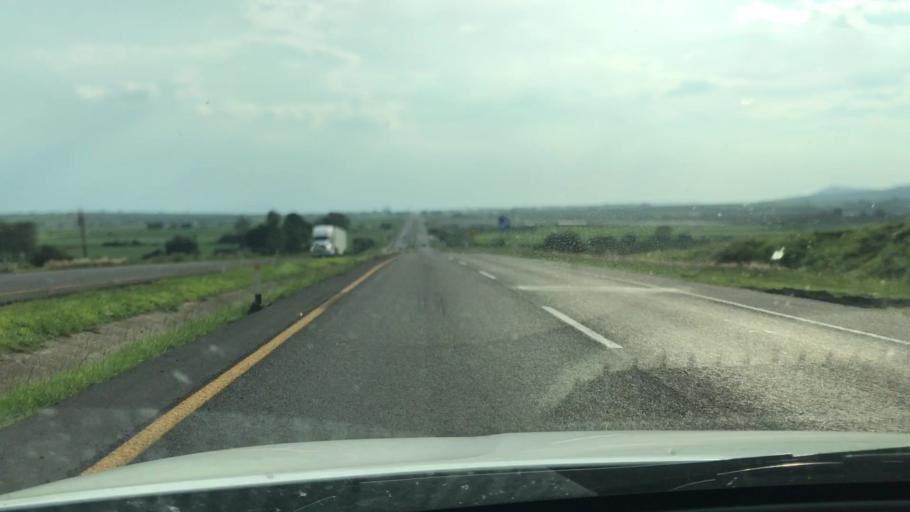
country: MX
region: Guanajuato
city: Penjamo
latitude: 20.3841
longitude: -101.7950
